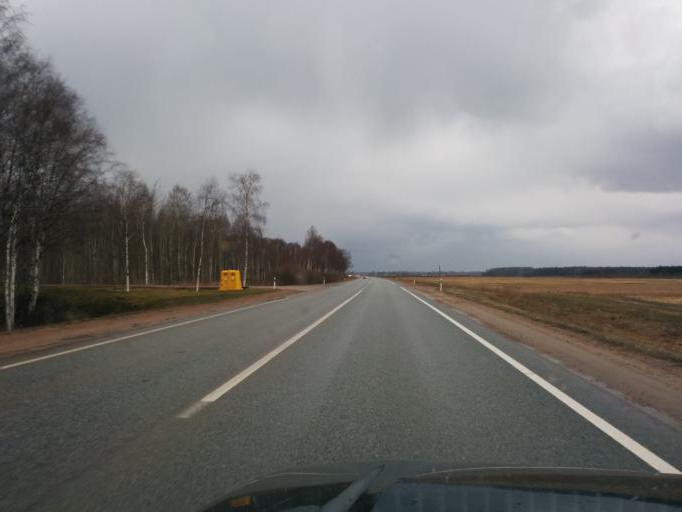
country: LV
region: Marupe
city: Marupe
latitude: 56.8554
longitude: 23.9989
